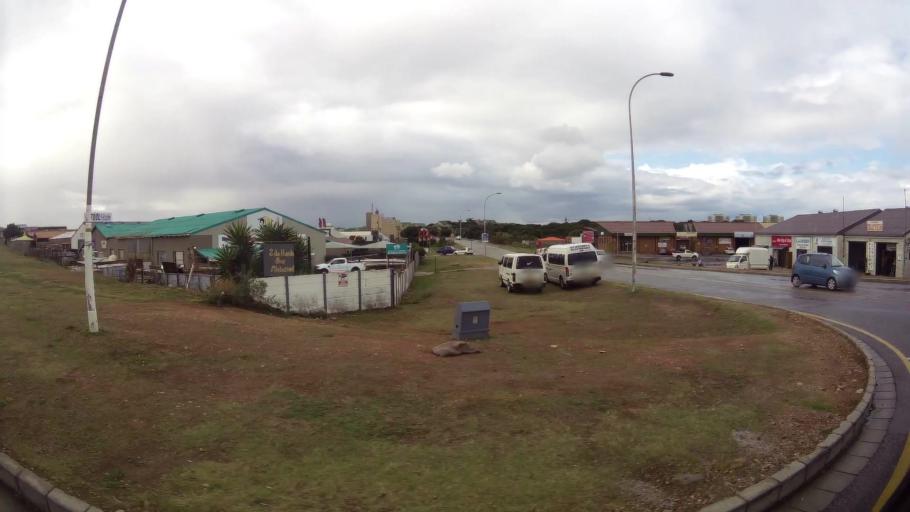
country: ZA
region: Western Cape
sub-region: Eden District Municipality
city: Mossel Bay
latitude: -34.1559
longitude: 22.1025
